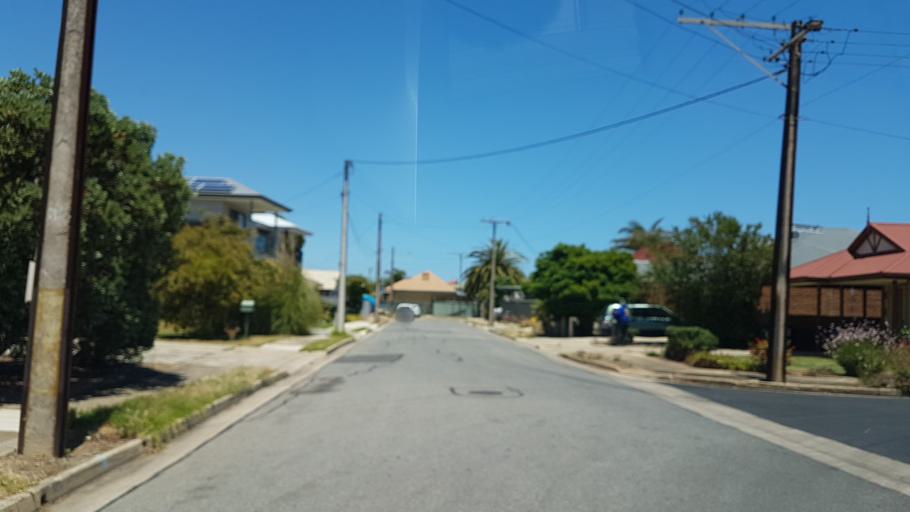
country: AU
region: South Australia
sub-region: Charles Sturt
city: West Lakes Shore
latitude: -34.8540
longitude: 138.4844
